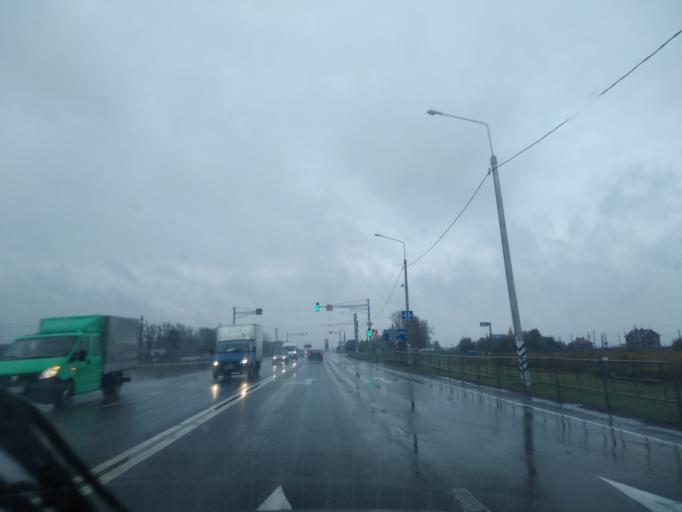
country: RU
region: Tula
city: Shchekino
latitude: 53.9977
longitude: 37.4740
